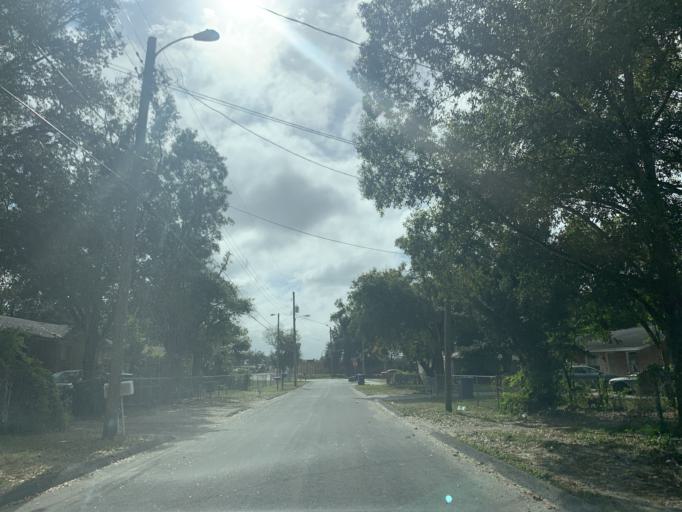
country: US
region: Florida
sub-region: Hillsborough County
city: East Lake-Orient Park
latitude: 27.9751
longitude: -82.3986
